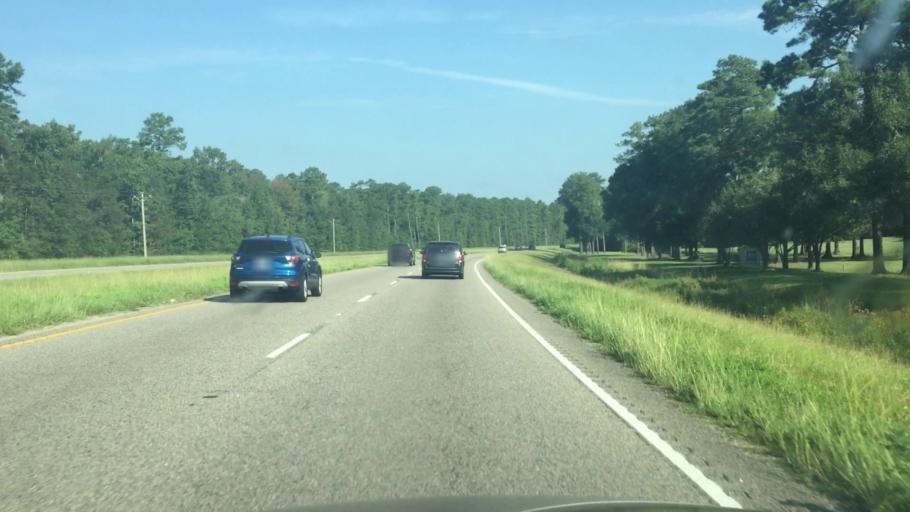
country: US
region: South Carolina
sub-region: Horry County
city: North Myrtle Beach
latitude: 33.9172
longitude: -78.7219
